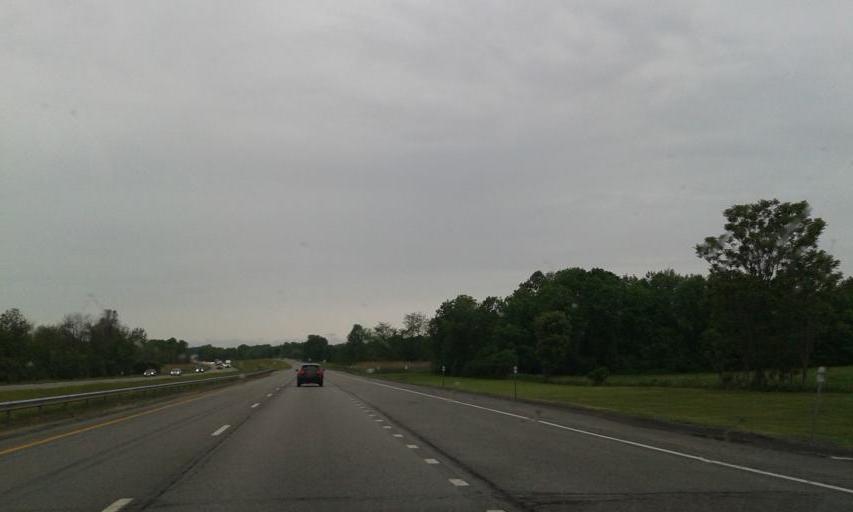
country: US
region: New York
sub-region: Genesee County
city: Bergen
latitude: 43.0303
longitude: -77.9091
